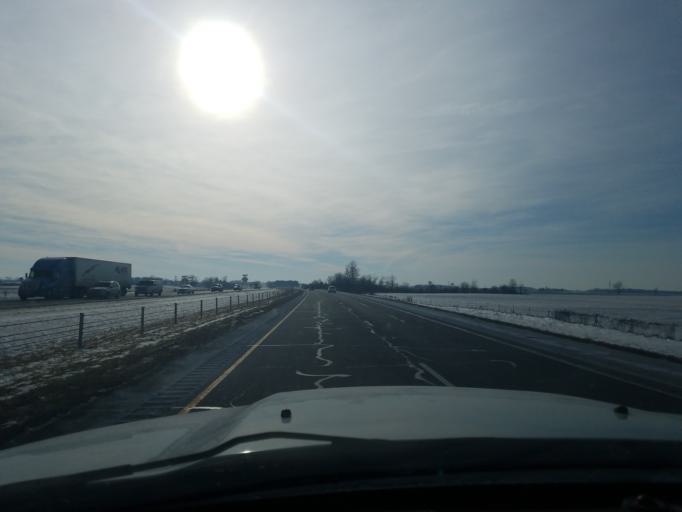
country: US
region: Indiana
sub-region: Huntington County
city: Warren
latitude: 40.6913
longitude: -85.4732
